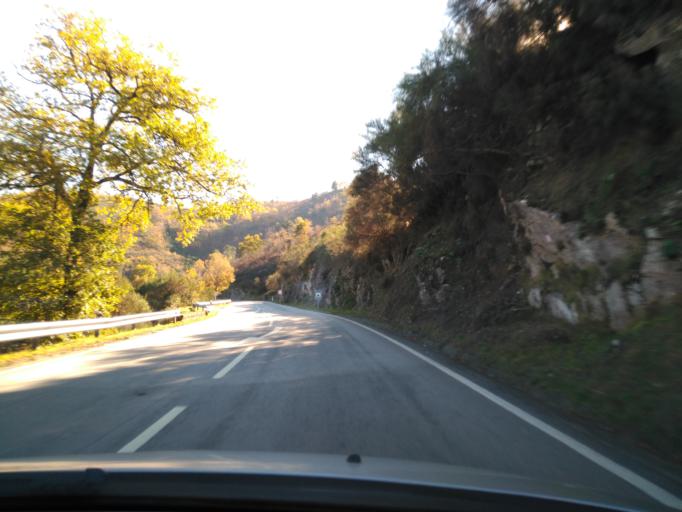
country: PT
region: Braga
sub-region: Vieira do Minho
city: Vieira do Minho
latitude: 41.6812
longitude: -8.0038
